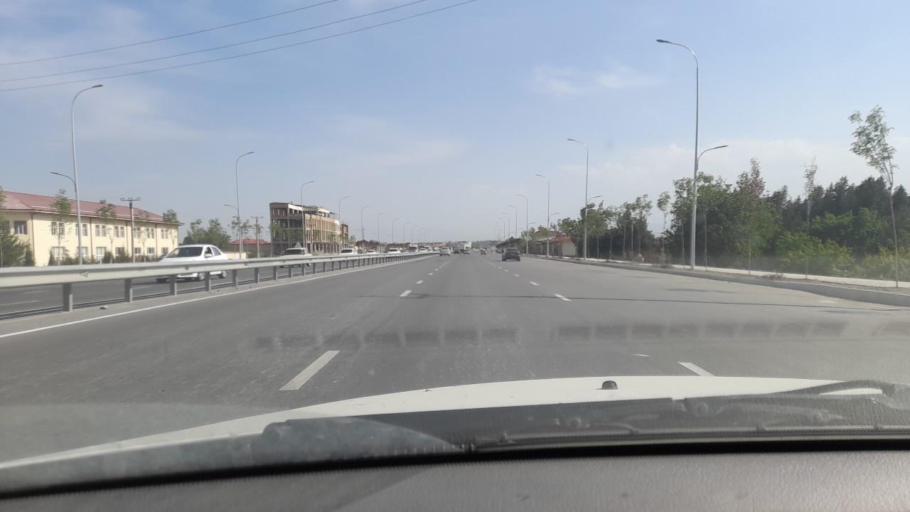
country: UZ
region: Samarqand
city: Daxbet
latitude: 39.7179
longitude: 66.9489
